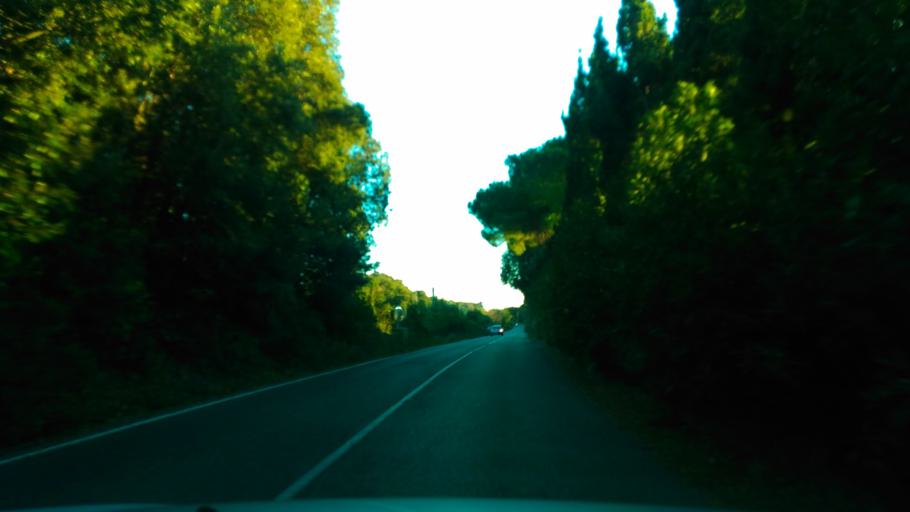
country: IT
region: Tuscany
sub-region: Provincia di Livorno
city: Quercianella
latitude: 43.4403
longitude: 10.3860
